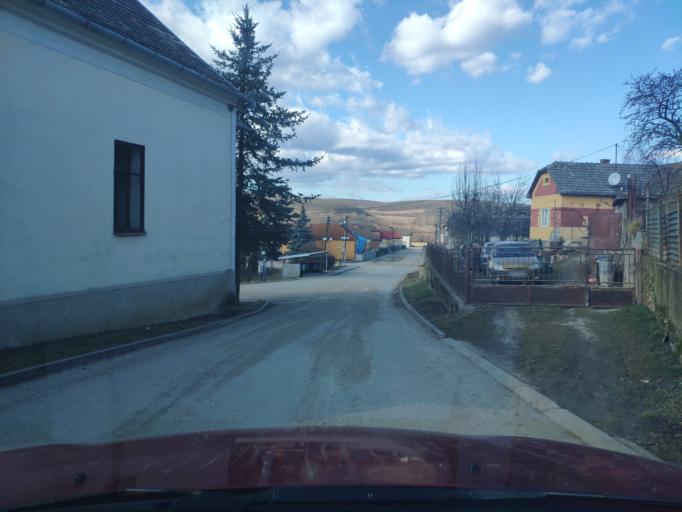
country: HU
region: Borsod-Abauj-Zemplen
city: Putnok
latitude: 48.4944
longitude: 20.3752
